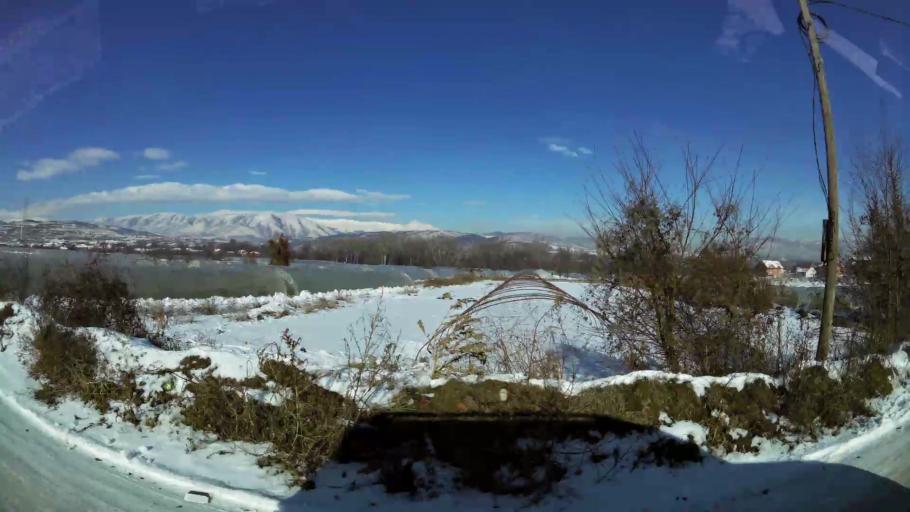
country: MK
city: Grchec
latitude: 41.9914
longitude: 21.3382
